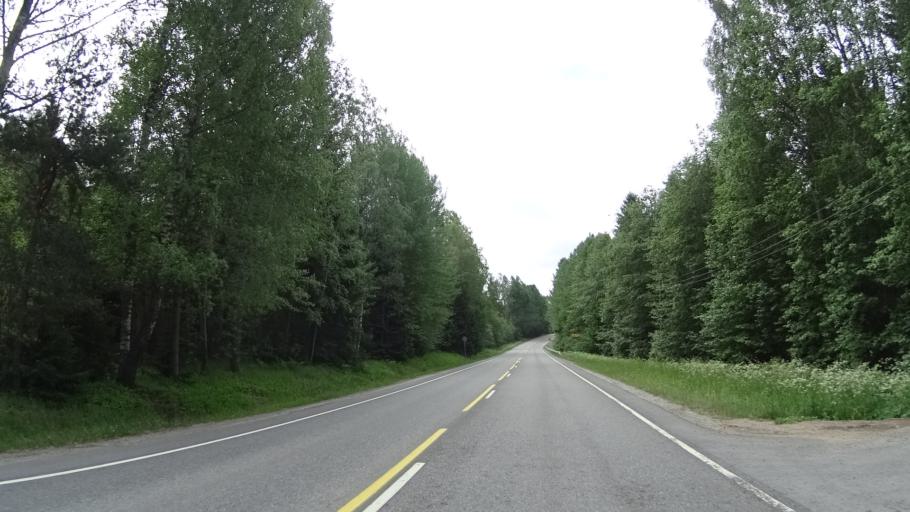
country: FI
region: Uusimaa
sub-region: Helsinki
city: Vihti
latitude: 60.2861
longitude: 24.4069
